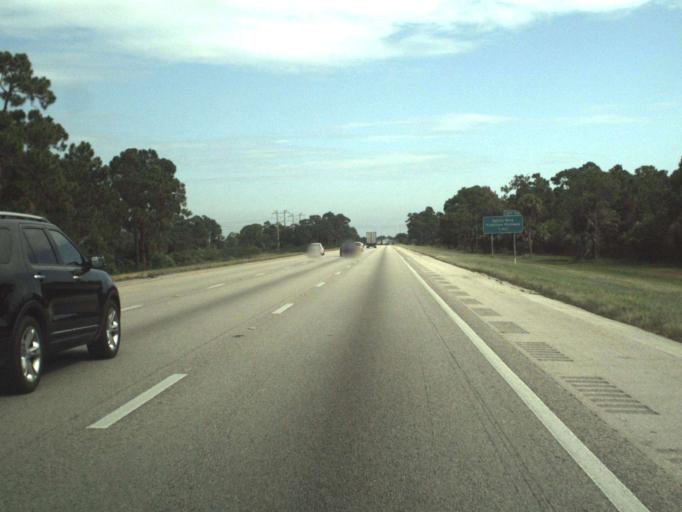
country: US
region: Florida
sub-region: Saint Lucie County
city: Port Saint Lucie
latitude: 27.2431
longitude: -80.4128
